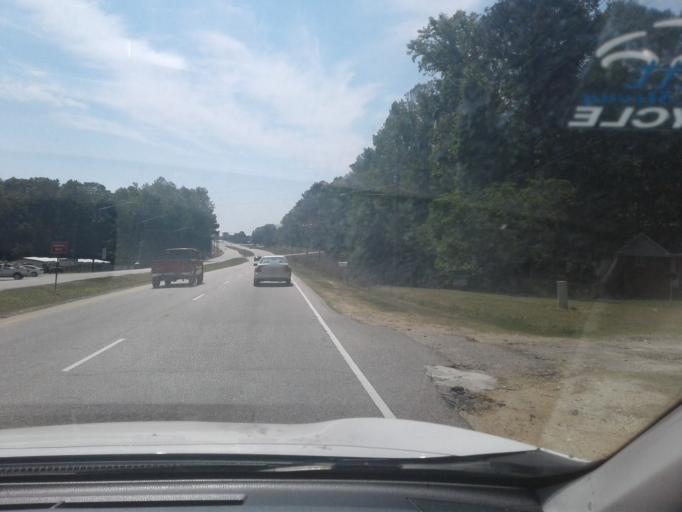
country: US
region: North Carolina
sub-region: Harnett County
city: Erwin
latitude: 35.3348
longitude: -78.6731
